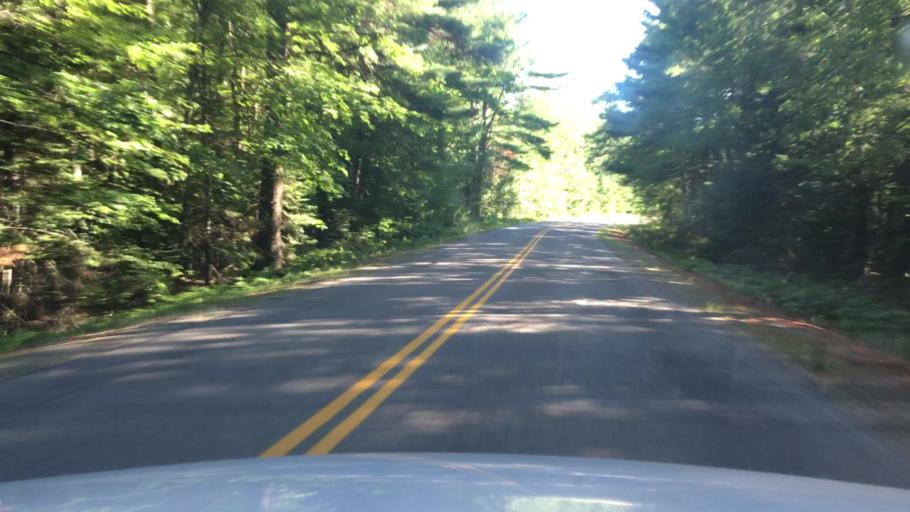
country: US
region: Maine
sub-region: Penobscot County
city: Enfield
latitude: 45.1927
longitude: -68.6067
